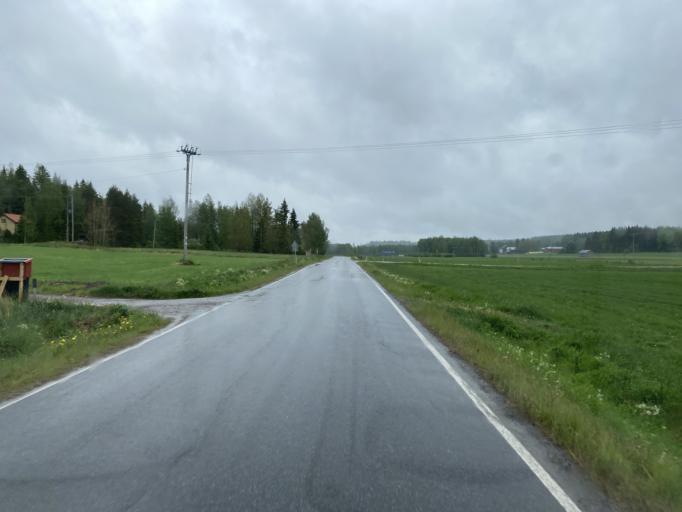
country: FI
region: Haeme
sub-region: Forssa
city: Humppila
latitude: 61.0426
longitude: 23.3929
